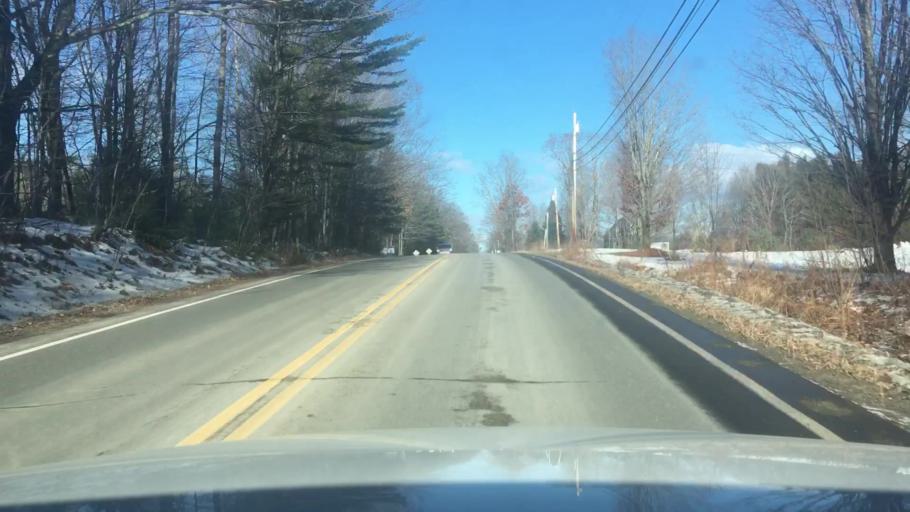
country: US
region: Maine
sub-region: Somerset County
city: Fairfield
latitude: 44.6534
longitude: -69.6766
